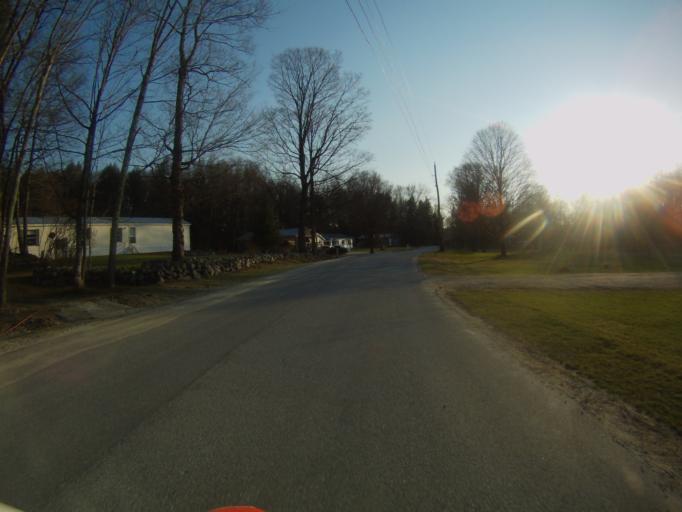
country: US
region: Vermont
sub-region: Addison County
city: Bristol
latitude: 44.0801
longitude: -73.0824
